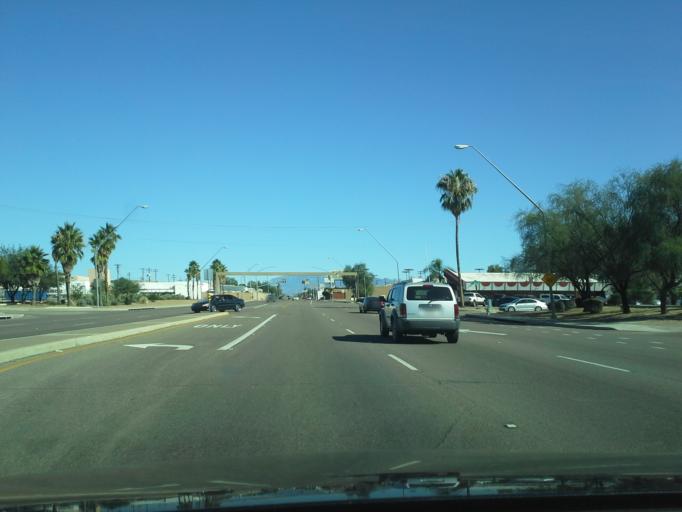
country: US
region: Arizona
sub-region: Pima County
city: South Tucson
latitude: 32.2213
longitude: -110.9587
